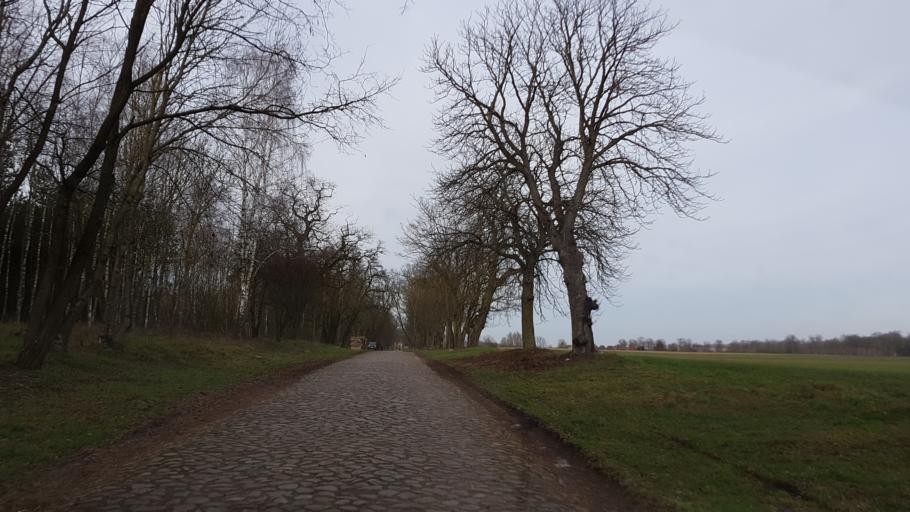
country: PL
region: Lubusz
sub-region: Powiat strzelecko-drezdenecki
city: Strzelce Krajenskie
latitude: 52.9243
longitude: 15.4167
